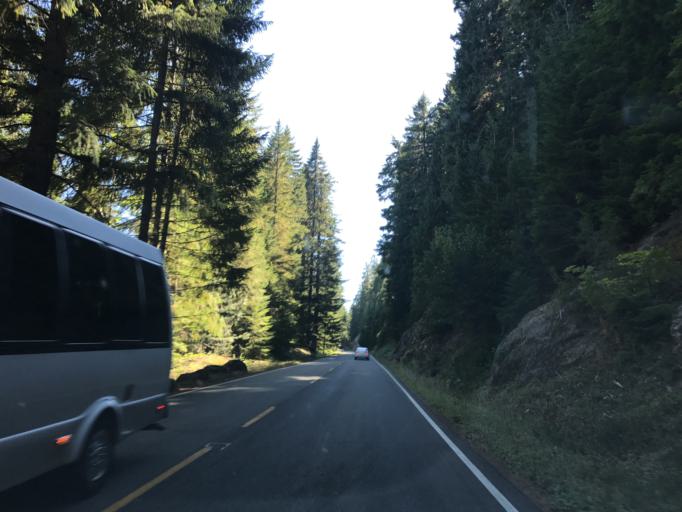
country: US
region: Washington
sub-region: Pierce County
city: Buckley
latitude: 46.7259
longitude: -121.5865
